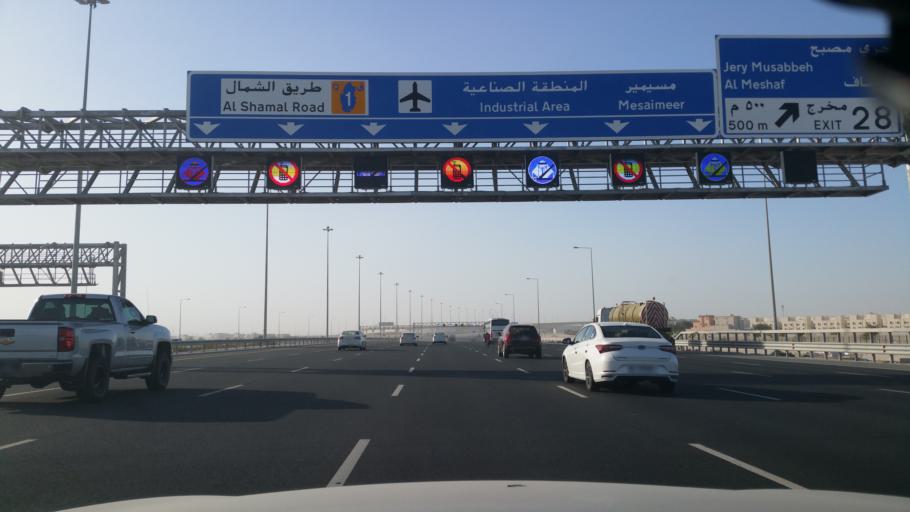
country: QA
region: Al Wakrah
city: Al Wukayr
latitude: 25.1735
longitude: 51.5563
